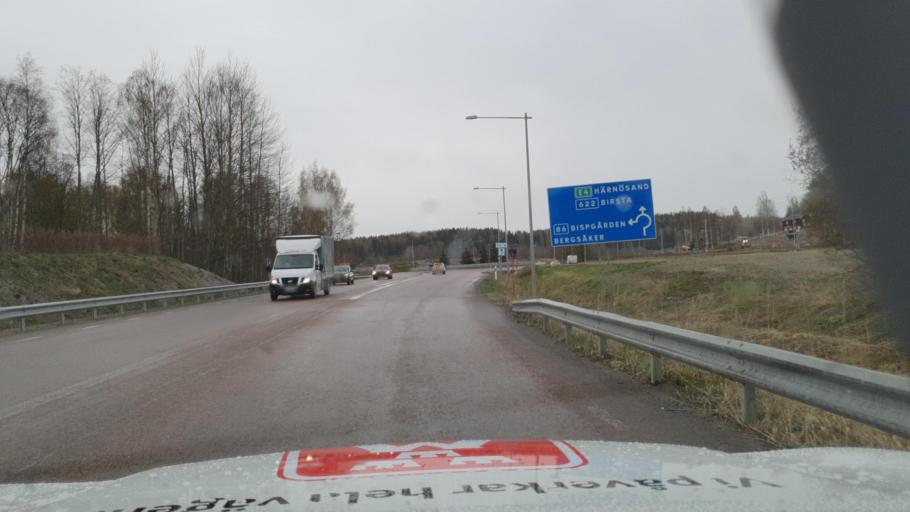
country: SE
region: Vaesternorrland
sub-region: Sundsvalls Kommun
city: Sundsvall
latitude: 62.4102
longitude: 17.2329
